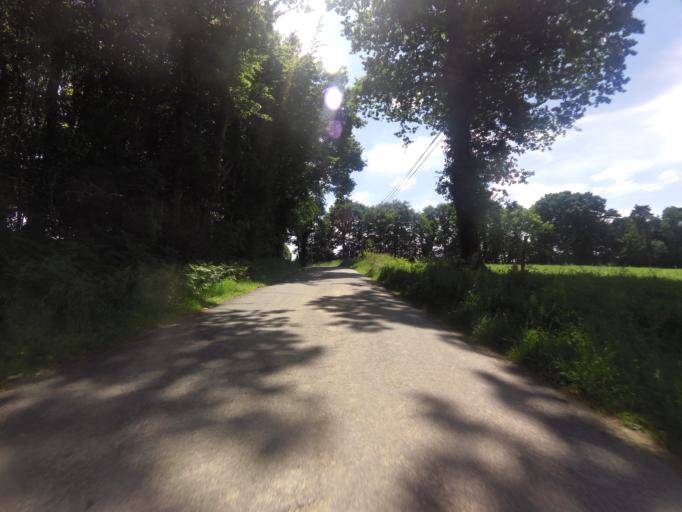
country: FR
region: Brittany
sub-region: Departement du Morbihan
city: Molac
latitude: 47.7245
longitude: -2.3959
